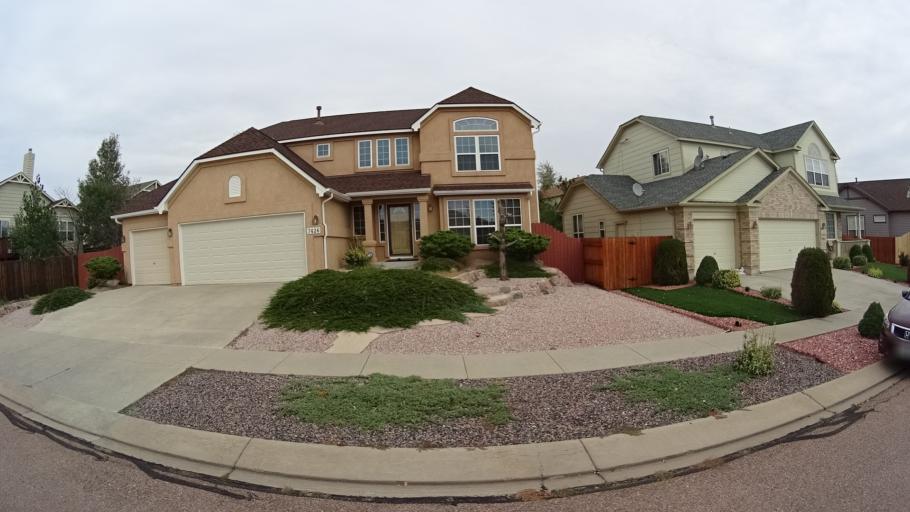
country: US
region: Colorado
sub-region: El Paso County
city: Cimarron Hills
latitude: 38.9134
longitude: -104.6896
